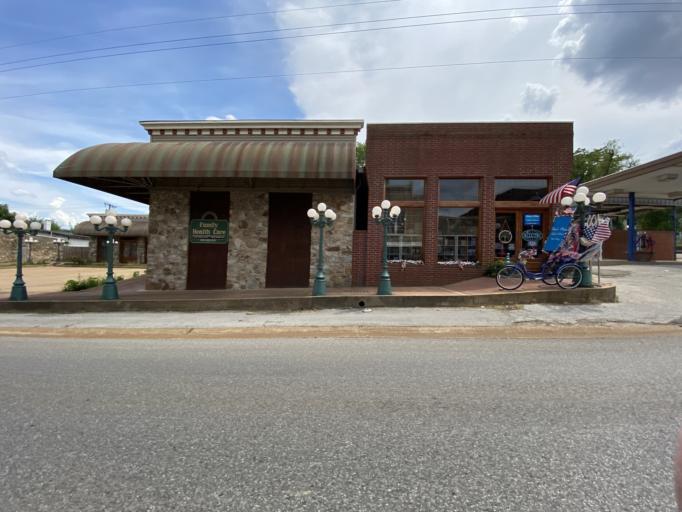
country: US
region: Missouri
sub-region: Oregon County
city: Thayer
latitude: 36.4957
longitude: -91.5413
